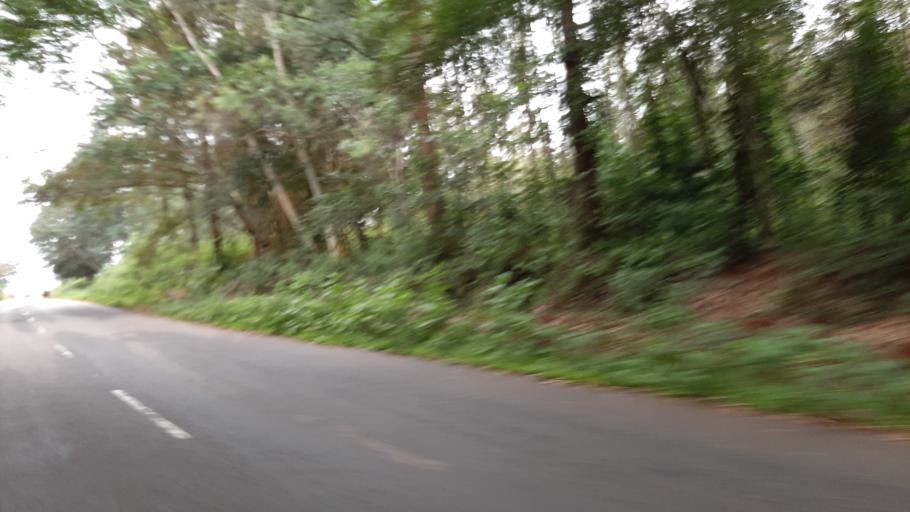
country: IN
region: Andhra Pradesh
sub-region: Vizianagaram District
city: Salur
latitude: 18.2885
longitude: 82.9285
